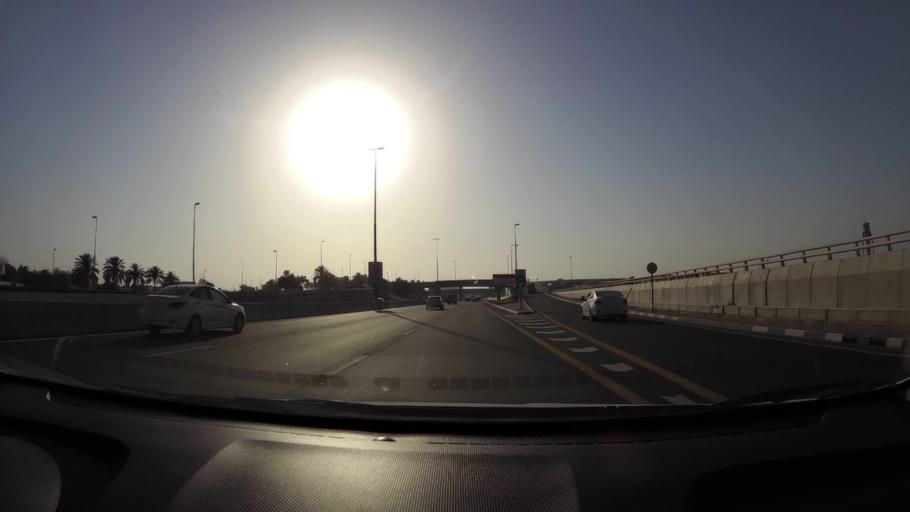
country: AE
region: Ash Shariqah
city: Sharjah
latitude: 25.2445
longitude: 55.3581
